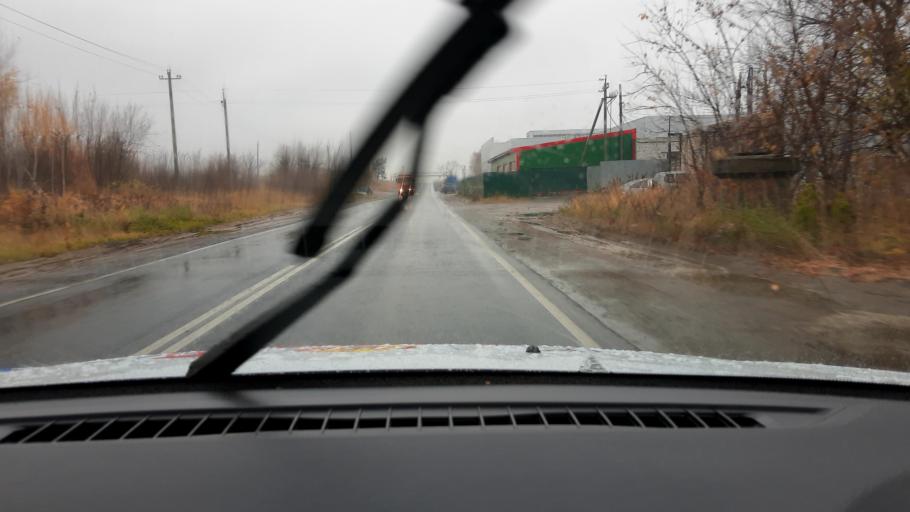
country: RU
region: Nizjnij Novgorod
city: Babino
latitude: 56.2624
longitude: 43.5934
